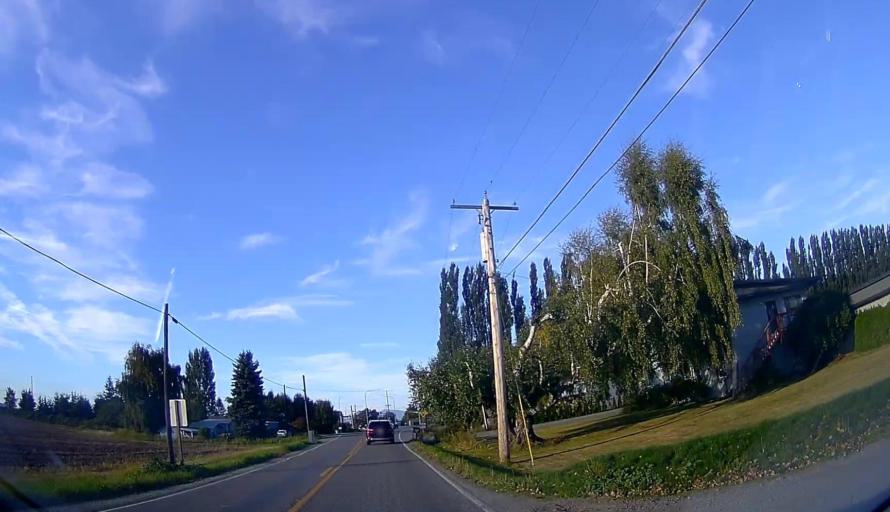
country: US
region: Washington
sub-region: Skagit County
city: Burlington
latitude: 48.4638
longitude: -122.3570
